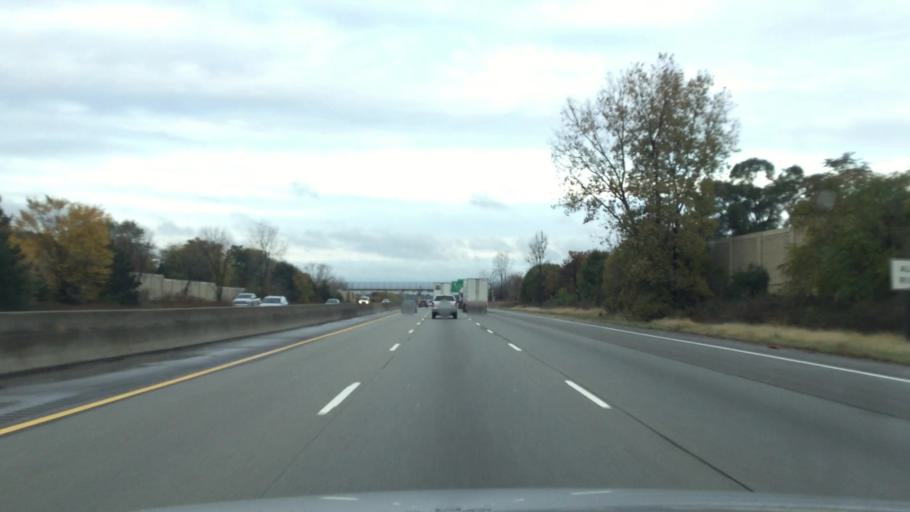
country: US
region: Michigan
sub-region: Washtenaw County
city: Ypsilanti
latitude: 42.2318
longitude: -83.5863
